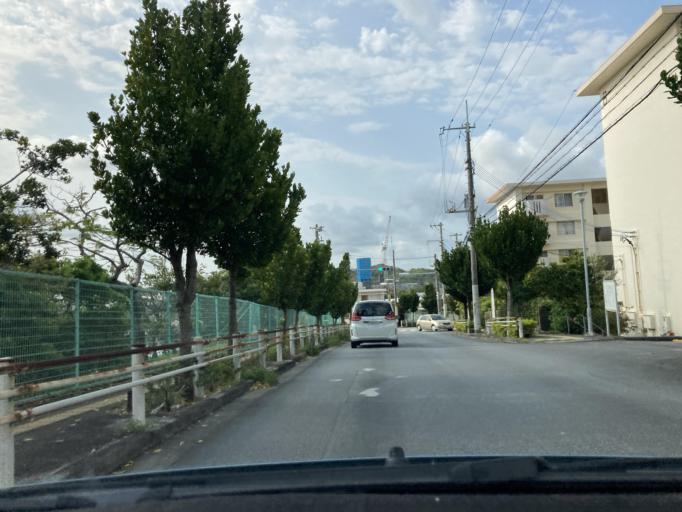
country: JP
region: Okinawa
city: Tomigusuku
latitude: 26.1982
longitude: 127.7212
